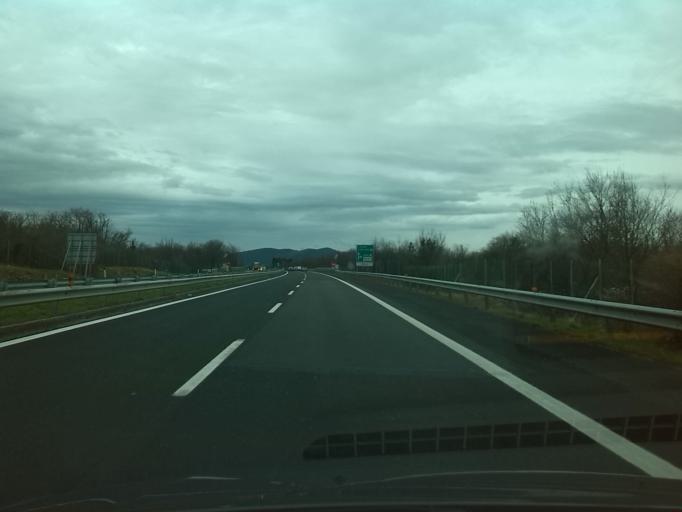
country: IT
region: Friuli Venezia Giulia
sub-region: Provincia di Trieste
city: Villa Opicina
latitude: 45.6793
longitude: 13.8169
